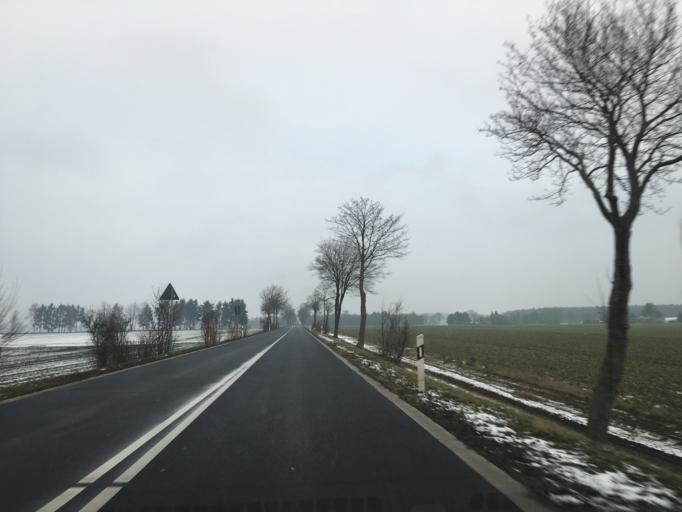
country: DE
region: North Rhine-Westphalia
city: Wegberg
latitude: 51.1323
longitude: 6.2311
